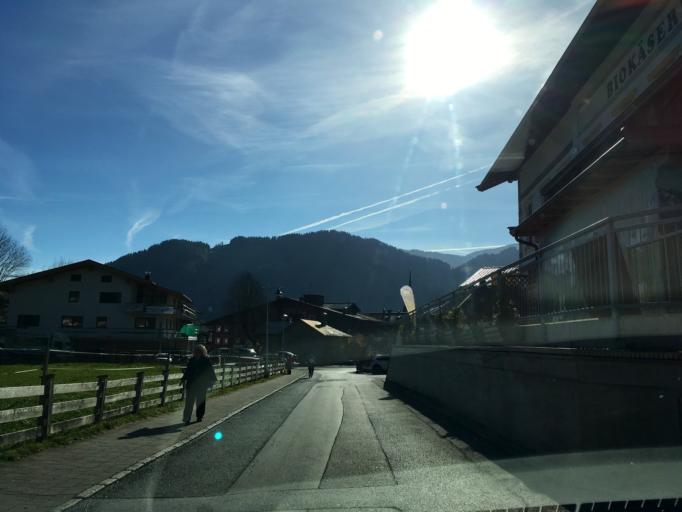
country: AT
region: Tyrol
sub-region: Politischer Bezirk Kufstein
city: Walchsee
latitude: 47.6527
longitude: 12.3175
